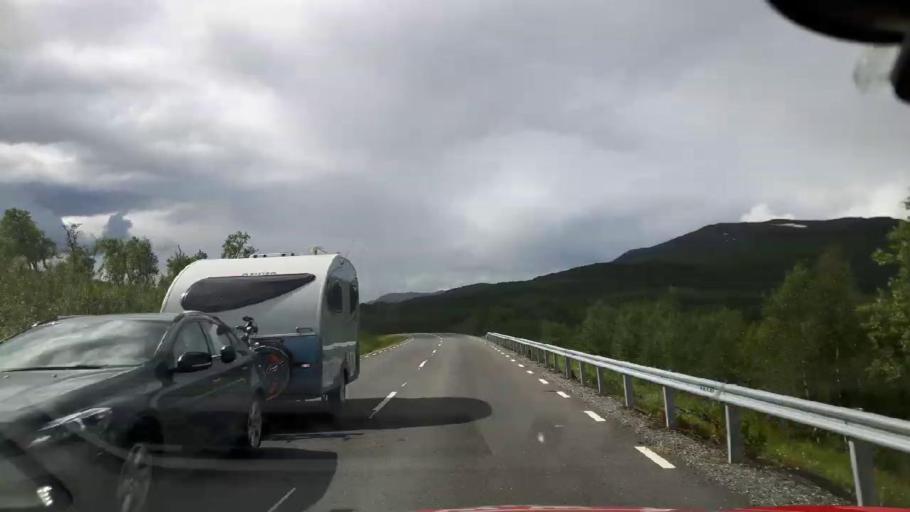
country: NO
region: Nordland
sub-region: Hattfjelldal
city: Hattfjelldal
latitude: 64.9889
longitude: 14.2178
